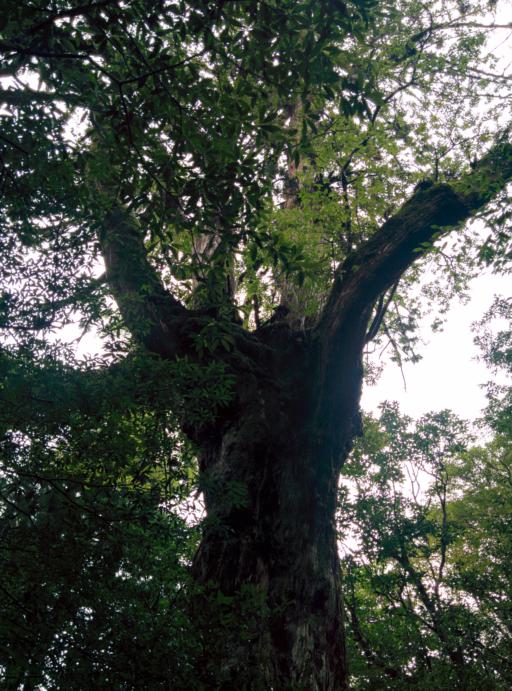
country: JP
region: Kagoshima
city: Nishinoomote
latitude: 30.3690
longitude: 130.5705
